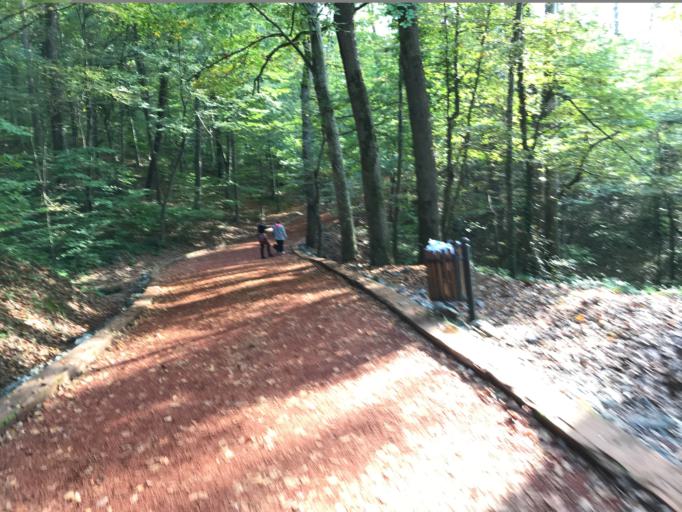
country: TR
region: Istanbul
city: Kemerburgaz
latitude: 41.1791
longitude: 28.9597
